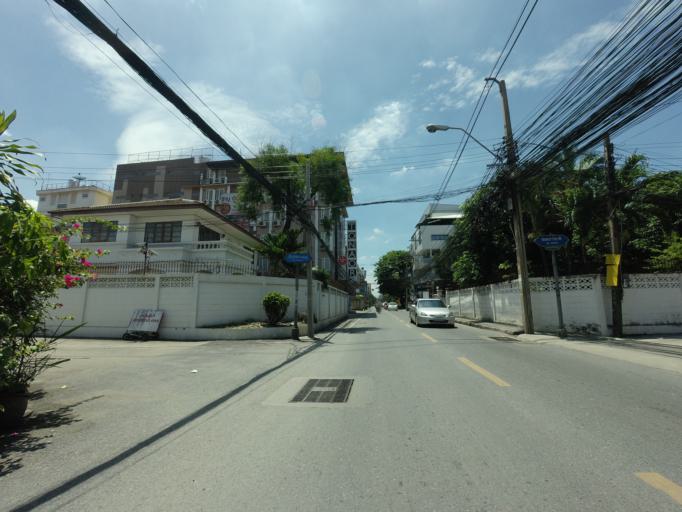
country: TH
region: Bangkok
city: Huai Khwang
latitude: 13.7896
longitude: 100.5781
